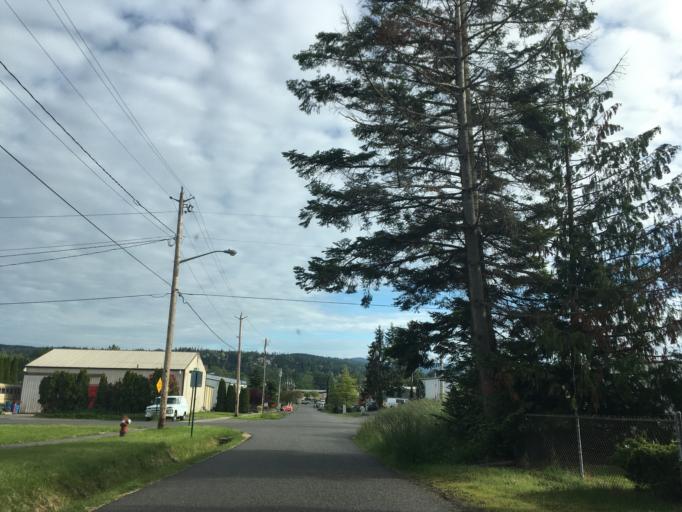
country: US
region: Washington
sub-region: Whatcom County
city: Bellingham
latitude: 48.7608
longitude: -122.4548
